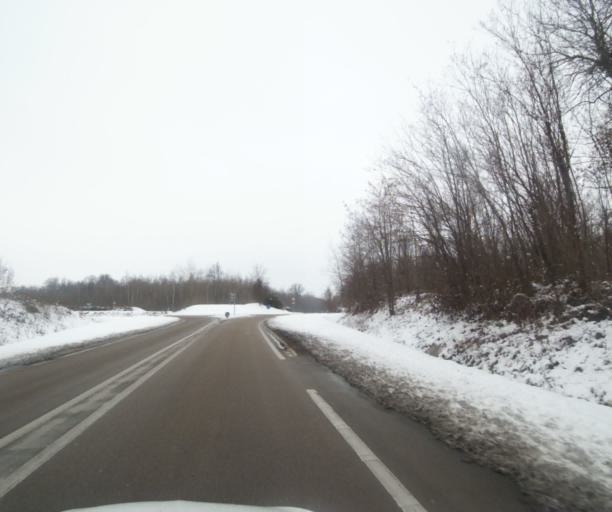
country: FR
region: Champagne-Ardenne
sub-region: Departement de la Haute-Marne
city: Saint-Dizier
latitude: 48.6061
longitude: 4.9109
